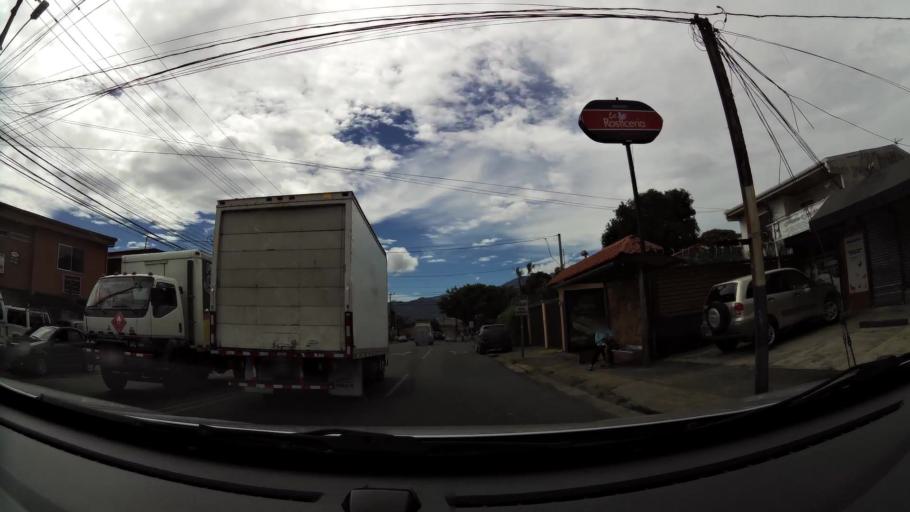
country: CR
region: San Jose
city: Curridabat
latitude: 9.9006
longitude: -84.0465
